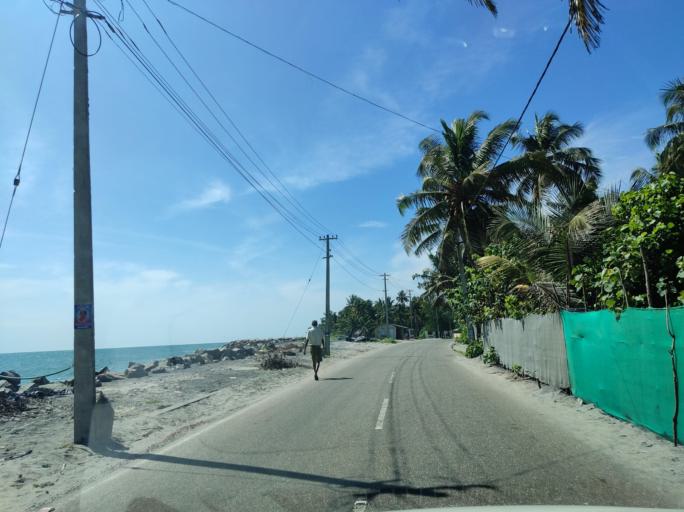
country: IN
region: Kerala
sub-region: Alappuzha
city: Kayankulam
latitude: 9.2027
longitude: 76.4333
